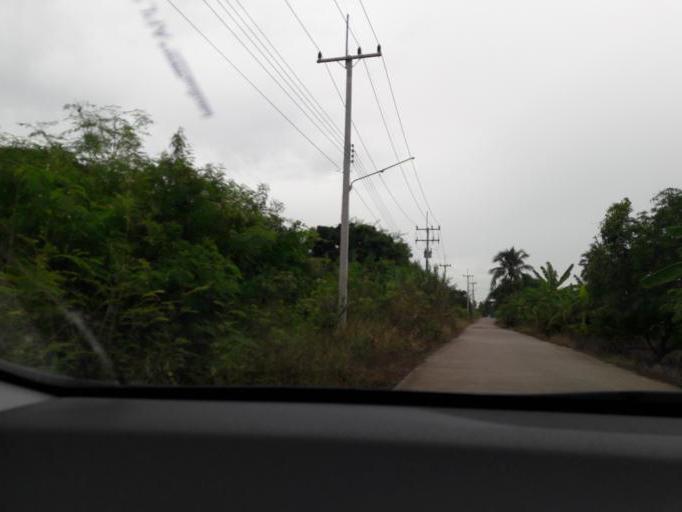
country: TH
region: Ratchaburi
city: Damnoen Saduak
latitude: 13.5675
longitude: 100.0116
